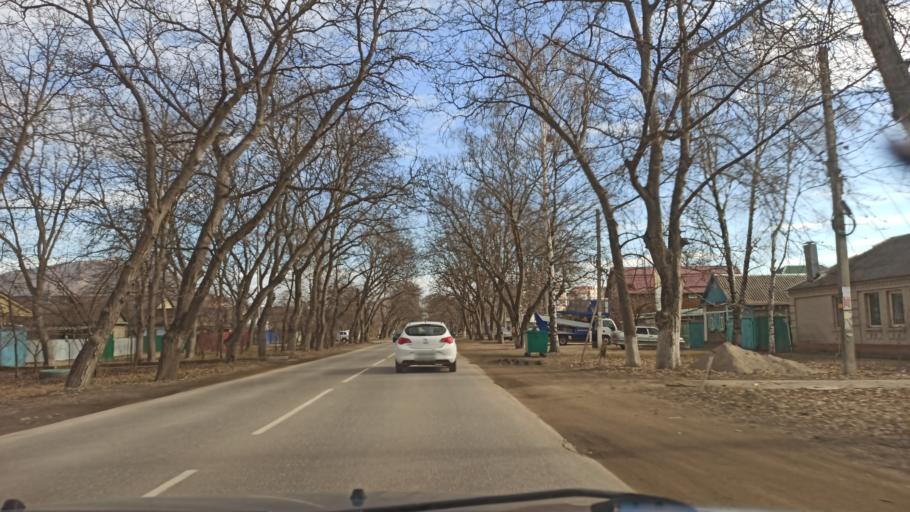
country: RU
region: Stavropol'skiy
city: Svobody
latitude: 44.0327
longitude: 43.0311
